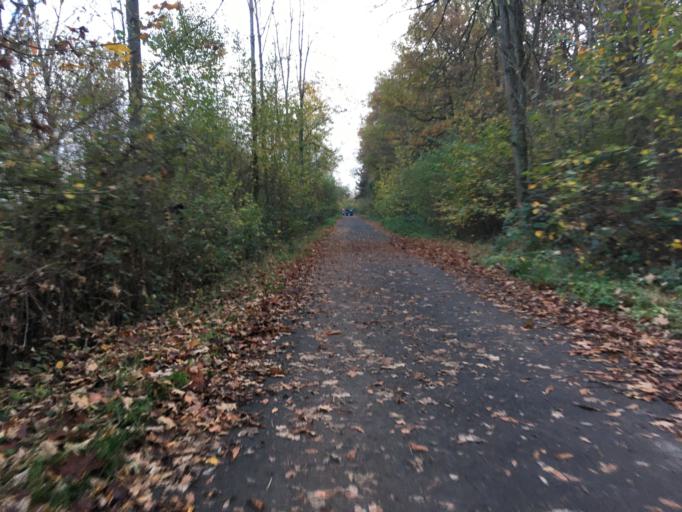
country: DE
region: Baden-Wuerttemberg
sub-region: Regierungsbezirk Stuttgart
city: Weinsberg
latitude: 49.1325
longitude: 9.2719
